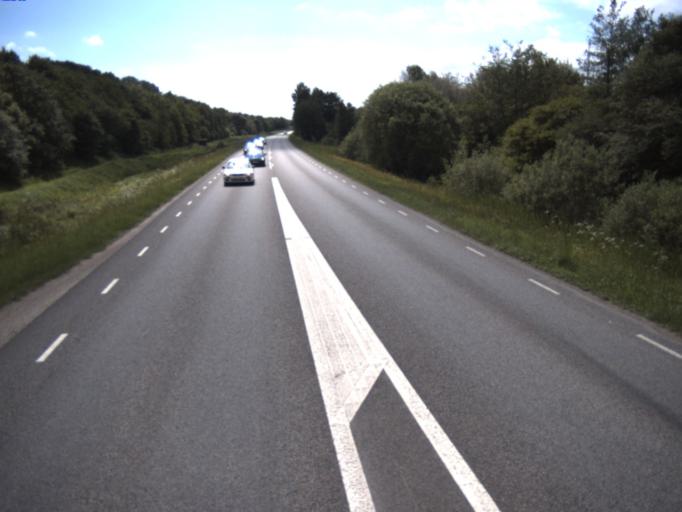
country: SE
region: Skane
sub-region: Helsingborg
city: Odakra
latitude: 56.0738
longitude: 12.7611
